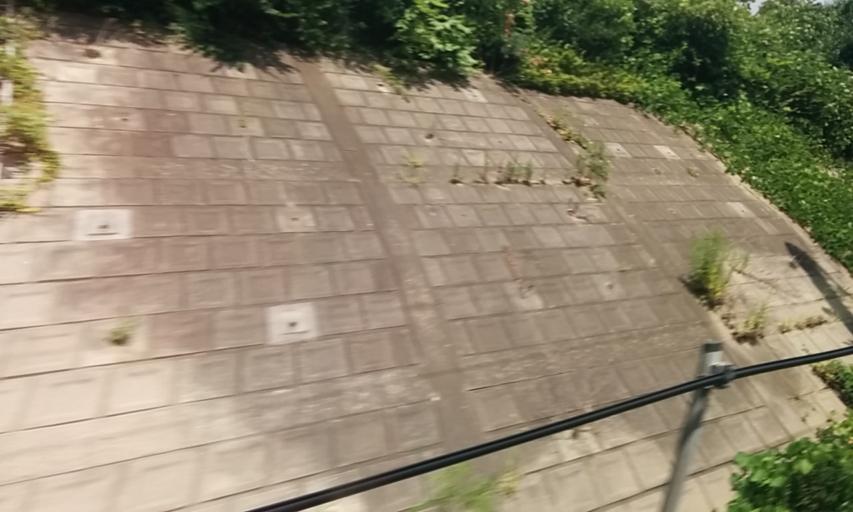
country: JP
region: Fukushima
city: Motomiya
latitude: 37.5192
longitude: 140.4338
